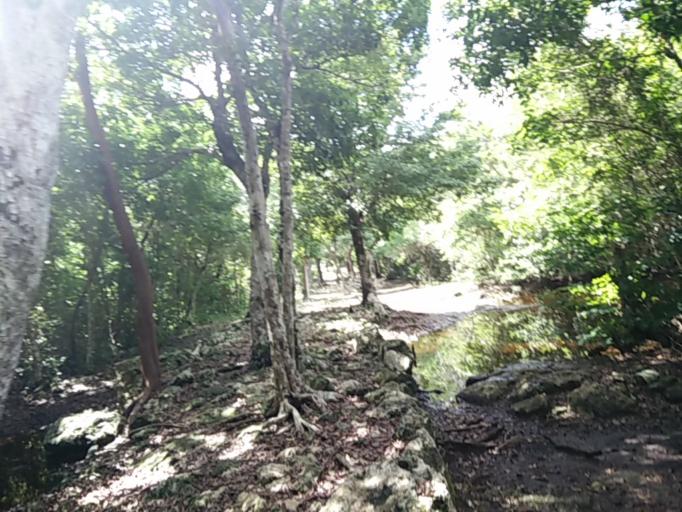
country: MX
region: Quintana Roo
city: San Miguel de Cozumel
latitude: 20.5020
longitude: -86.8439
